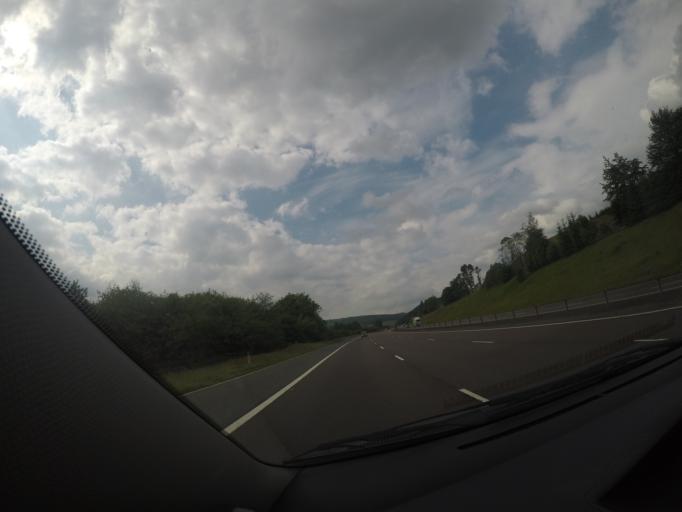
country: GB
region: Scotland
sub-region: Dumfries and Galloway
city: Moffat
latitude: 55.3473
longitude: -3.5032
